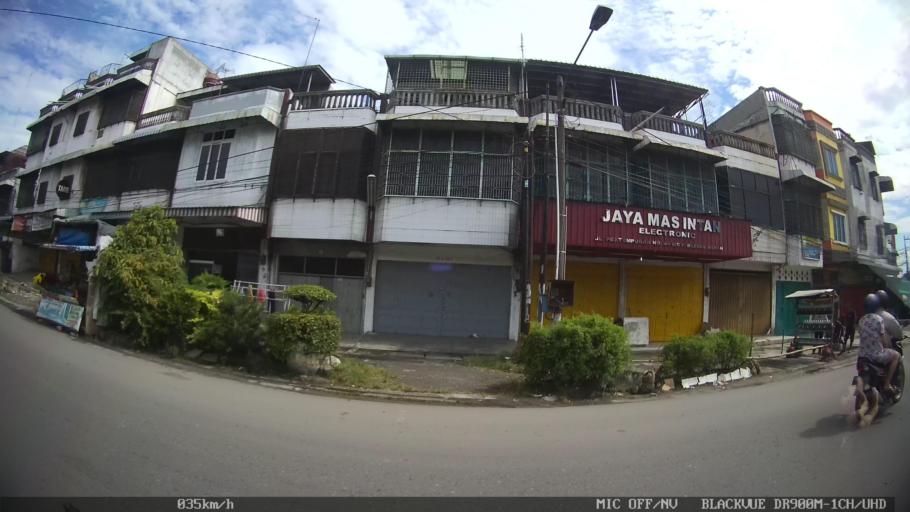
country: ID
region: North Sumatra
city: Medan
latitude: 3.6271
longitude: 98.6658
